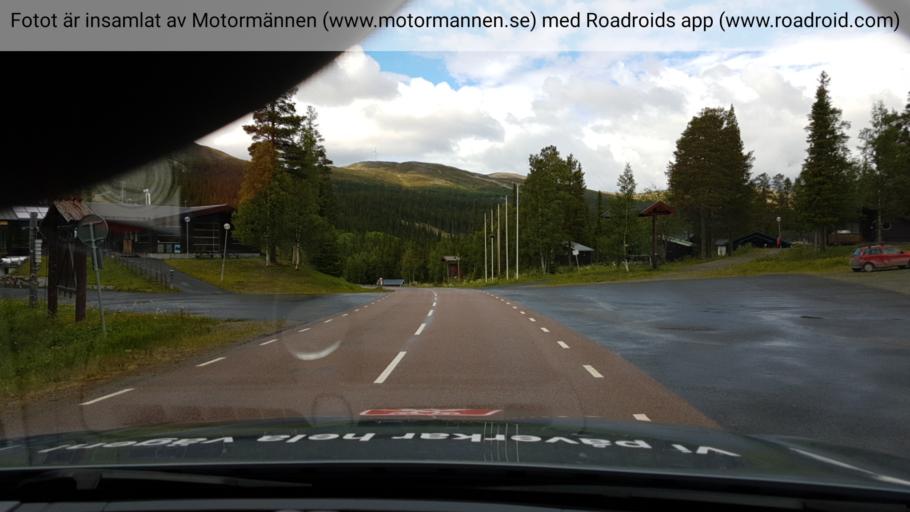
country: SE
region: Jaemtland
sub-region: Are Kommun
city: Jarpen
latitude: 63.0844
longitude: 13.7730
